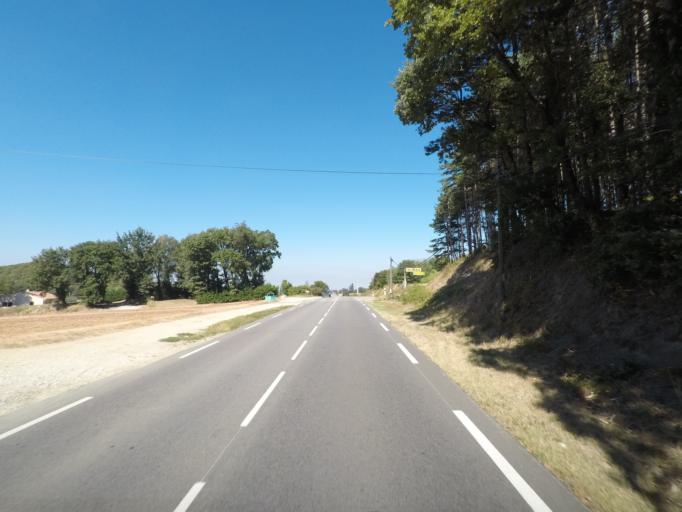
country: FR
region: Rhone-Alpes
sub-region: Departement de la Drome
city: Eurre
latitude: 44.7887
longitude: 5.0234
